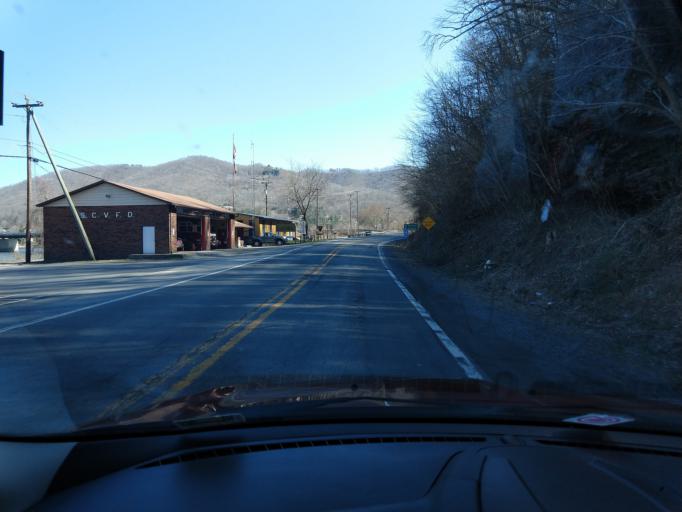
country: US
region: West Virginia
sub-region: Summers County
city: Hinton
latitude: 37.6517
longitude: -80.8897
